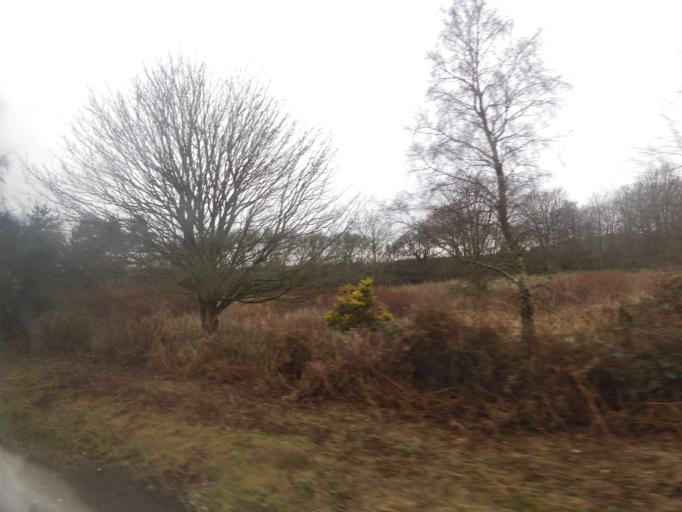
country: GB
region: England
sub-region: Norfolk
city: Briston
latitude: 52.9222
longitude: 1.1143
